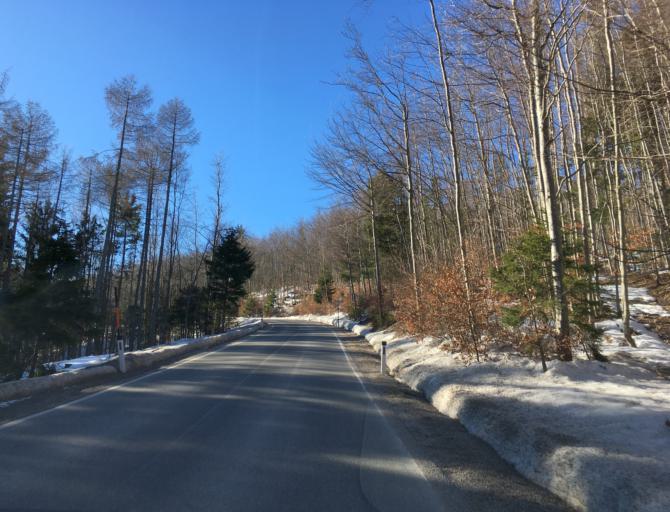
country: AT
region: Lower Austria
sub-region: Politischer Bezirk Wiener Neustadt
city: Waldegg
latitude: 47.8415
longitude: 16.0327
